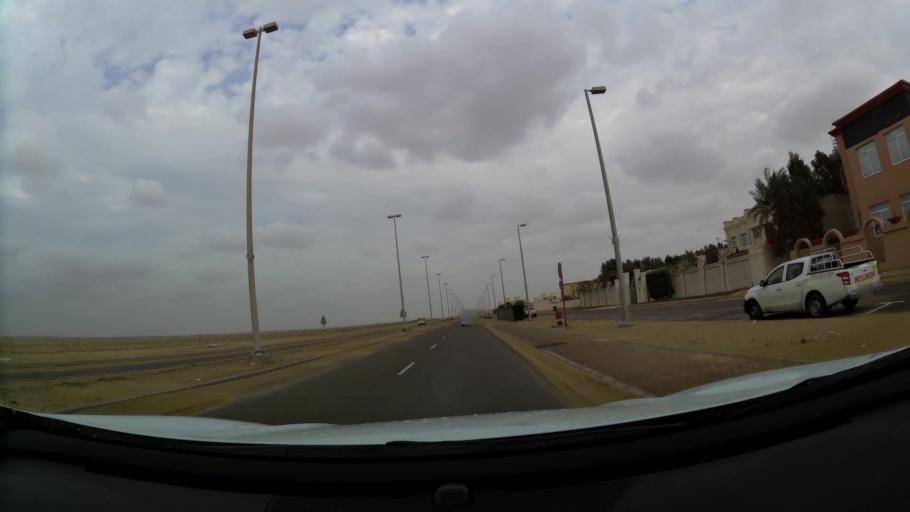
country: AE
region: Abu Dhabi
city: Abu Dhabi
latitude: 24.3583
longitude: 54.6143
